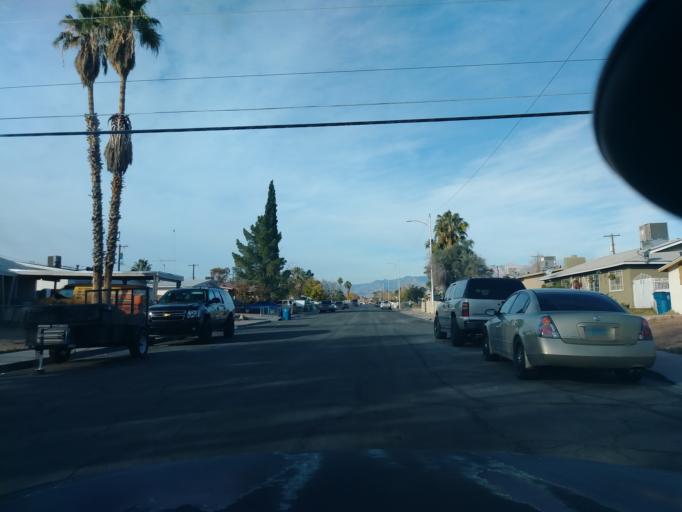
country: US
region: Nevada
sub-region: Clark County
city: Spring Valley
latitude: 36.1650
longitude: -115.2297
